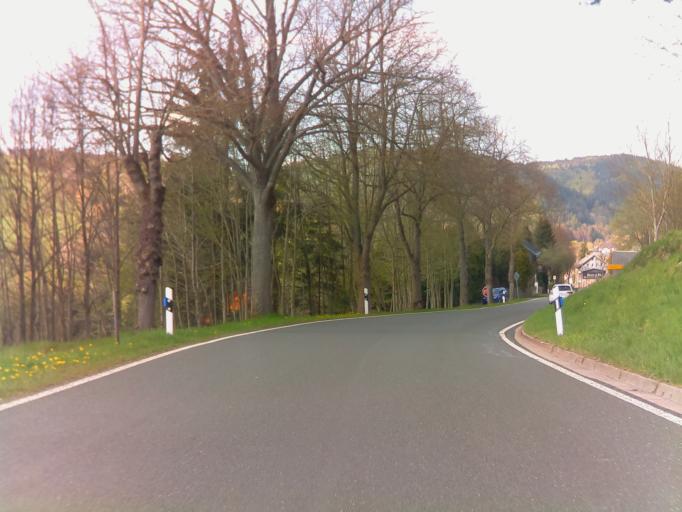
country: DE
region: Thuringia
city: Grafenthal
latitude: 50.5148
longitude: 11.2985
